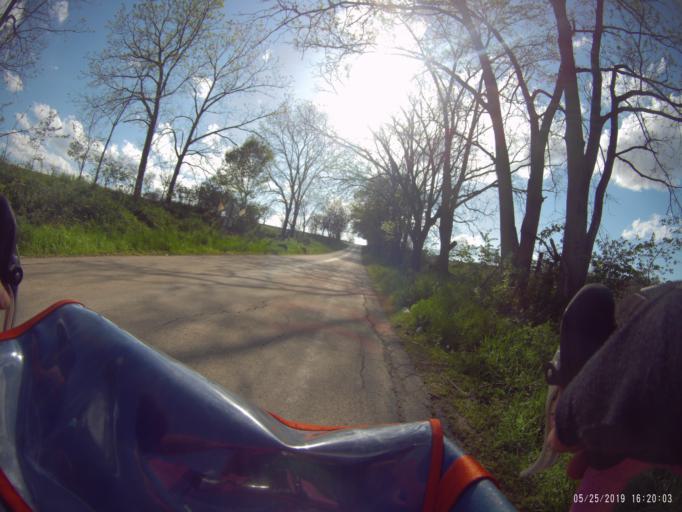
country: US
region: Wisconsin
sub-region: Dane County
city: Mount Horeb
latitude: 42.9664
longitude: -89.6989
